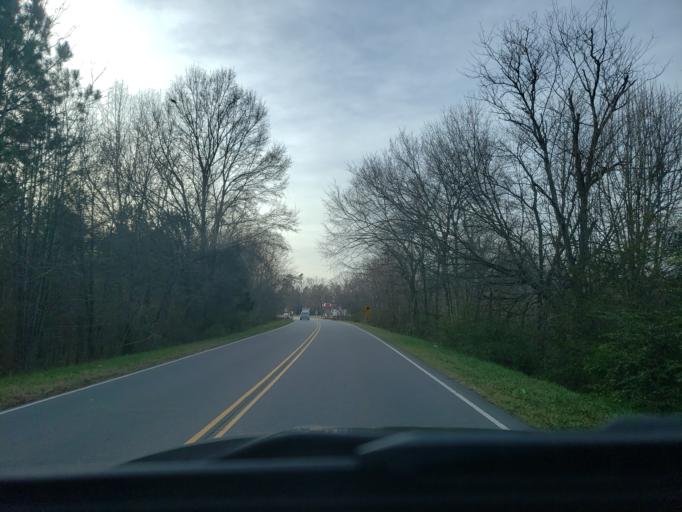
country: US
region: North Carolina
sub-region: Cleveland County
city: Boiling Springs
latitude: 35.3048
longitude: -81.7053
